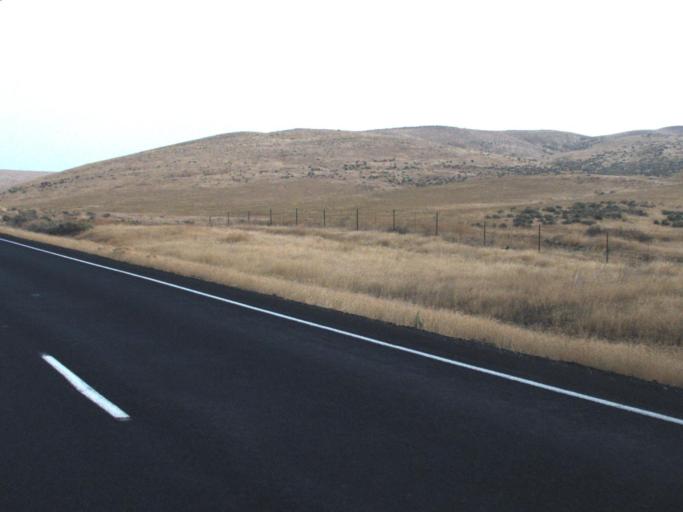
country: US
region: Washington
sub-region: Yakima County
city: Toppenish
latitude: 46.2679
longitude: -120.4034
